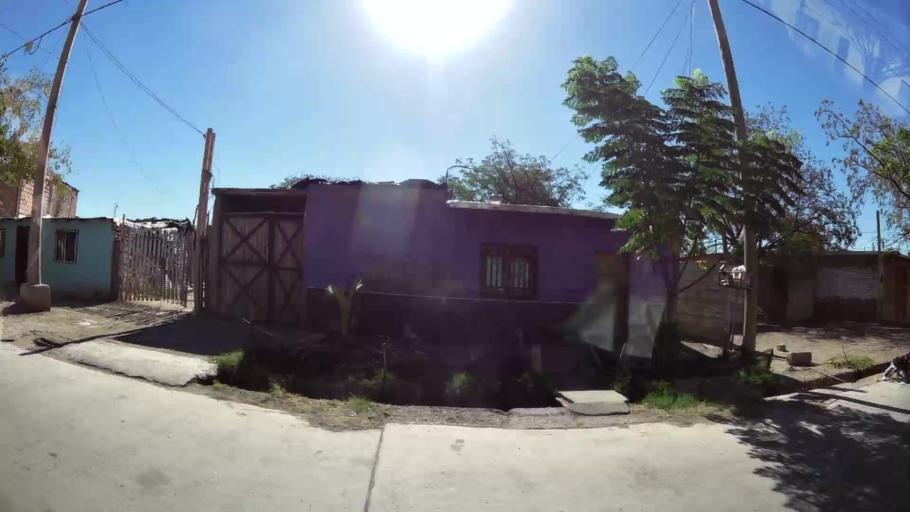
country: AR
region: Mendoza
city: Las Heras
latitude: -32.8373
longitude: -68.8171
